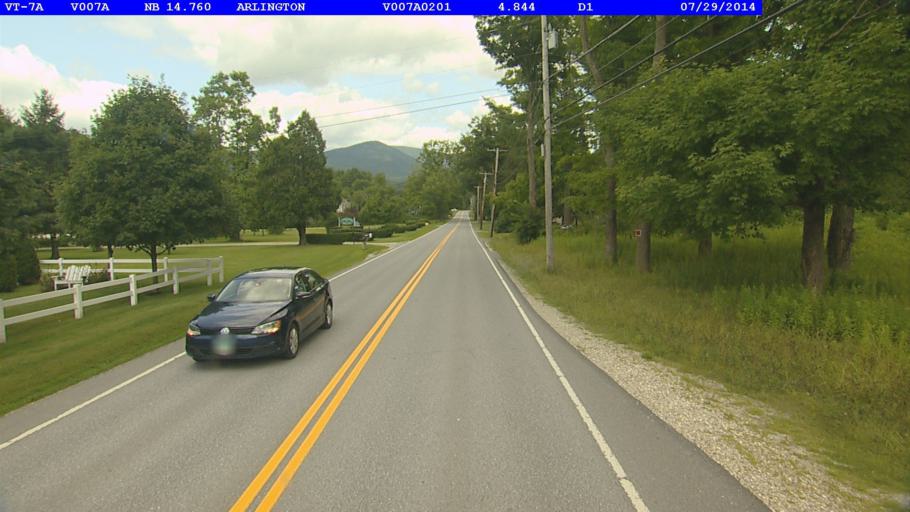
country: US
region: Vermont
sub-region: Bennington County
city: Arlington
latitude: 43.0856
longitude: -73.1434
